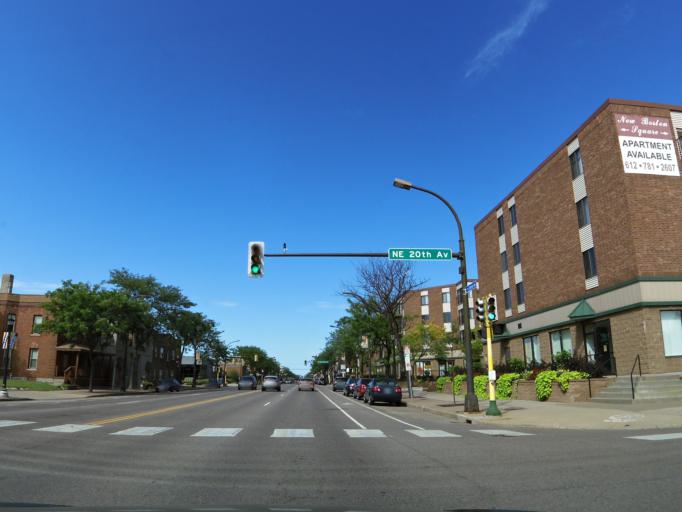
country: US
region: Minnesota
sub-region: Hennepin County
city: Saint Anthony
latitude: 45.0088
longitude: -93.2474
